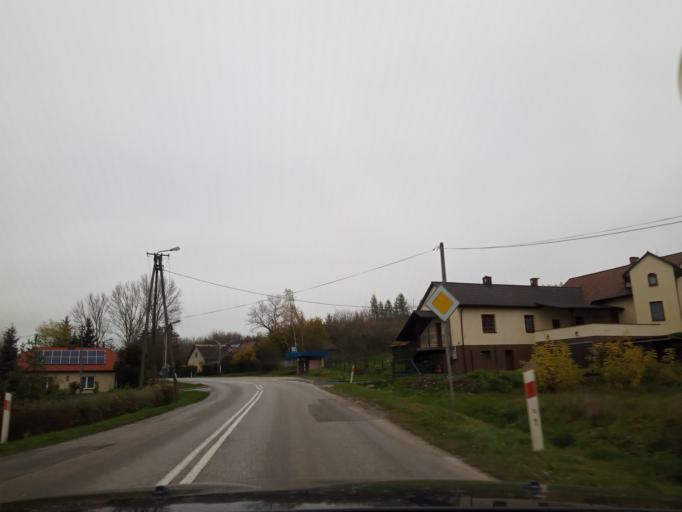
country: PL
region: Swietokrzyskie
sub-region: Powiat pinczowski
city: Dzialoszyce
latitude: 50.3826
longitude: 20.3348
